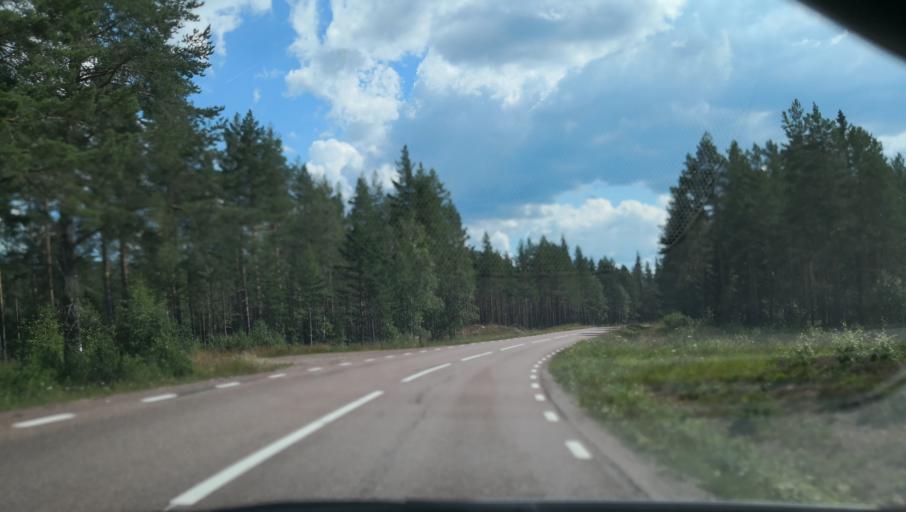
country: SE
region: Dalarna
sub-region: Rattviks Kommun
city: Vikarbyn
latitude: 61.1515
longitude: 15.0995
